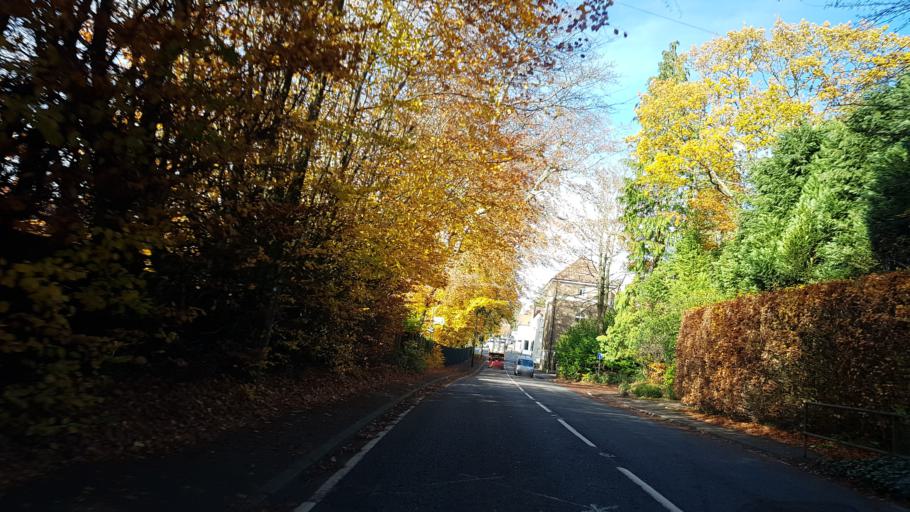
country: GB
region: England
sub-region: Surrey
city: Hindhead
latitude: 51.1126
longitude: -0.7321
